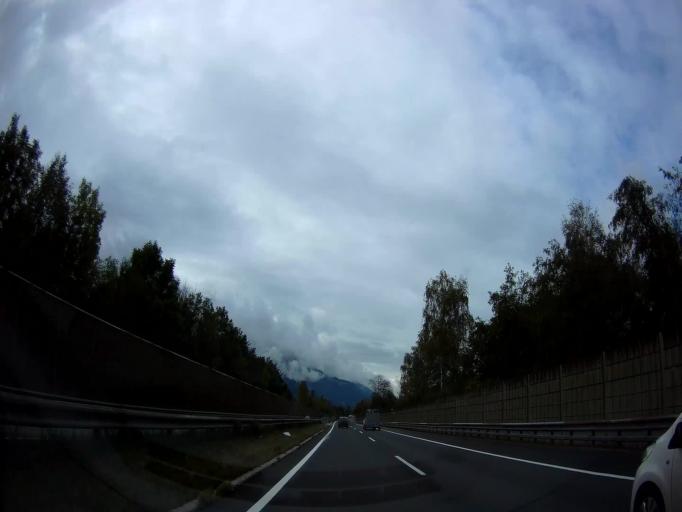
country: AT
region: Tyrol
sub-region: Politischer Bezirk Schwaz
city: Weer
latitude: 47.3129
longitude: 11.6365
